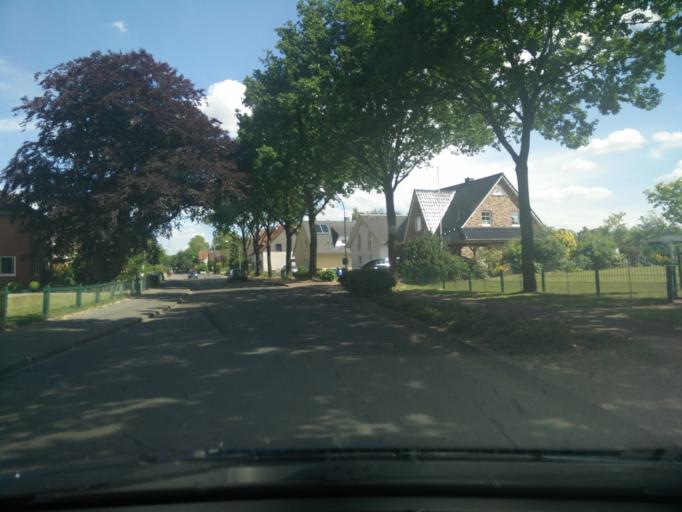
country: DE
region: Schleswig-Holstein
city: Prisdorf
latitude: 53.6789
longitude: 9.7576
